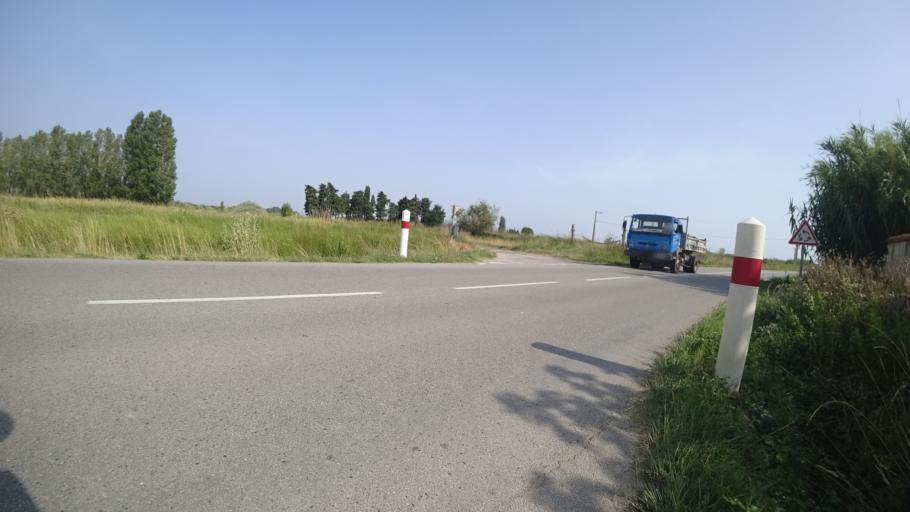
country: FR
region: Languedoc-Roussillon
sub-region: Departement des Pyrenees-Orientales
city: Sainte-Marie-Plage
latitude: 42.7307
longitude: 3.0127
